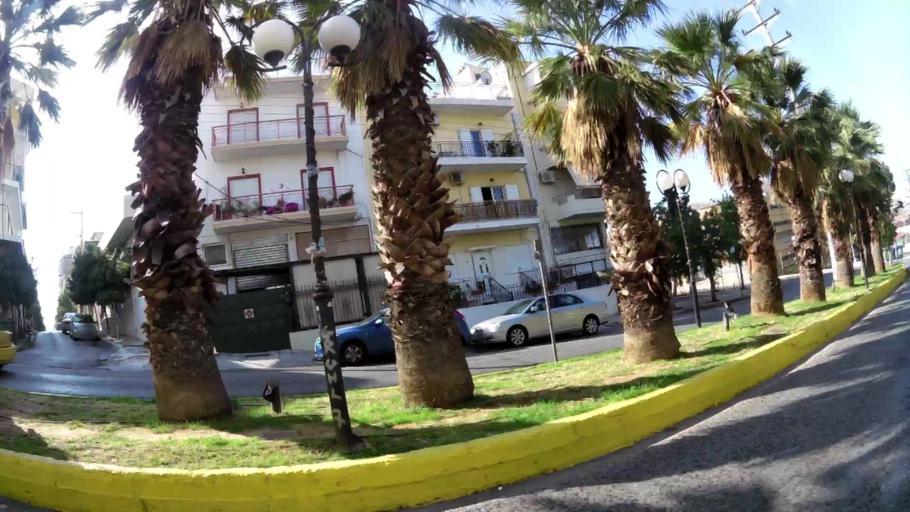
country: GR
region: Attica
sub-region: Nomos Piraios
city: Drapetsona
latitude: 37.9537
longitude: 23.6143
